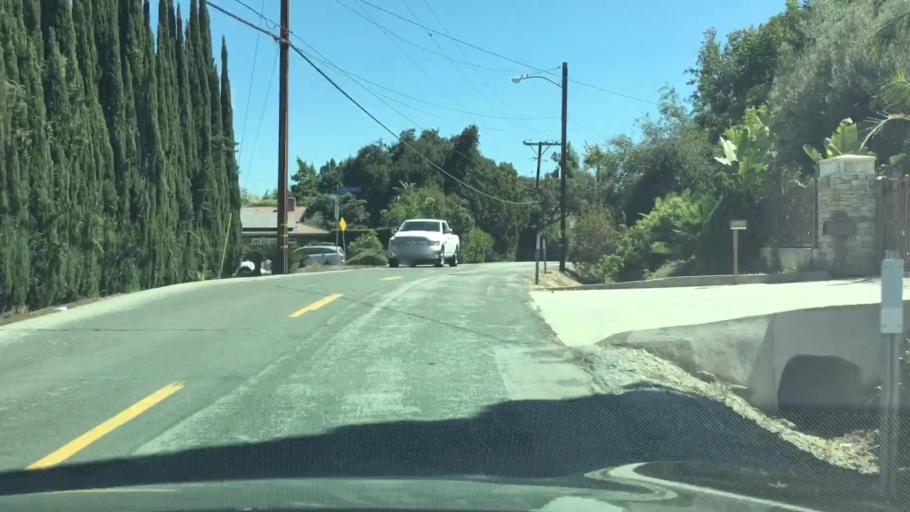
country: US
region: California
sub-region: Los Angeles County
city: Hacienda Heights
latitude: 34.0074
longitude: -117.9890
